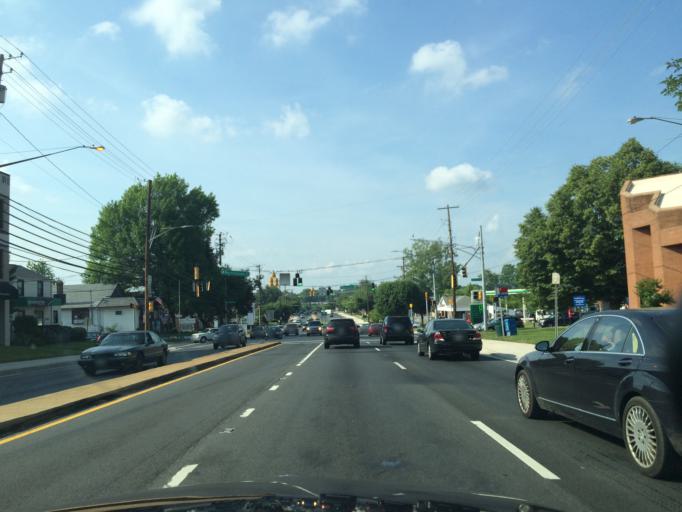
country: US
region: Maryland
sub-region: Montgomery County
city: Olney
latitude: 39.1498
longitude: -77.0668
